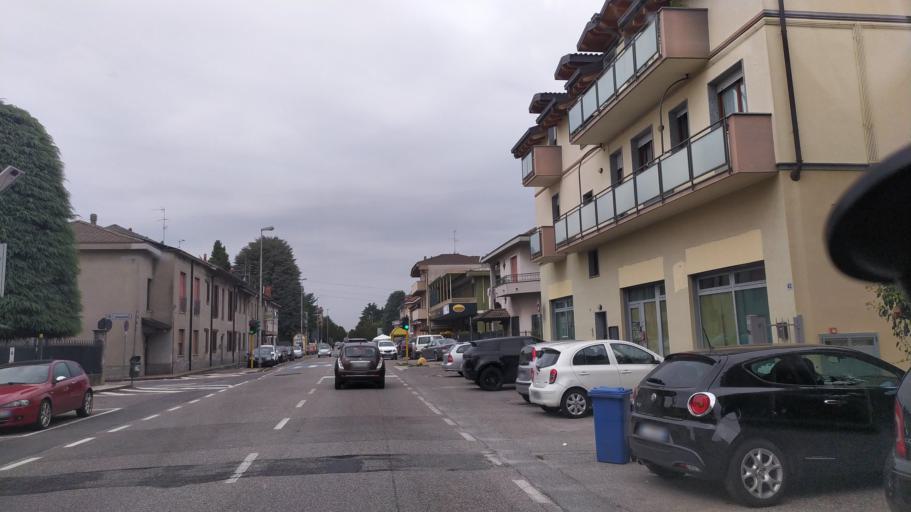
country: IT
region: Lombardy
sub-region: Provincia di Monza e Brianza
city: Seregno
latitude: 45.6399
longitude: 9.1831
